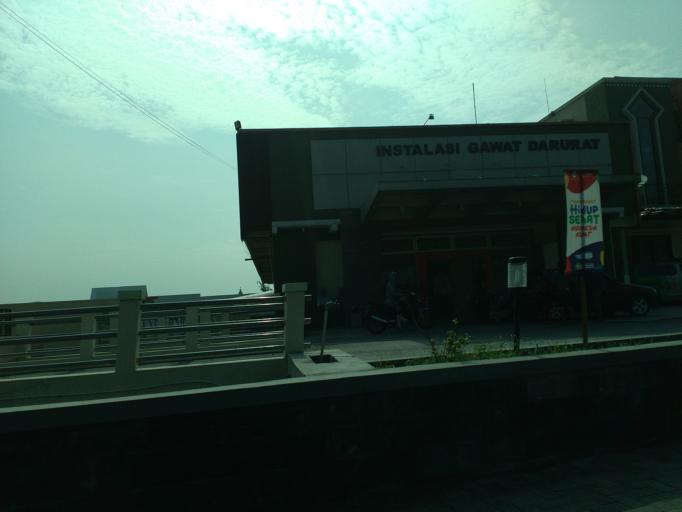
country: ID
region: Central Java
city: Delanggu
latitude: -7.6137
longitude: 110.7010
